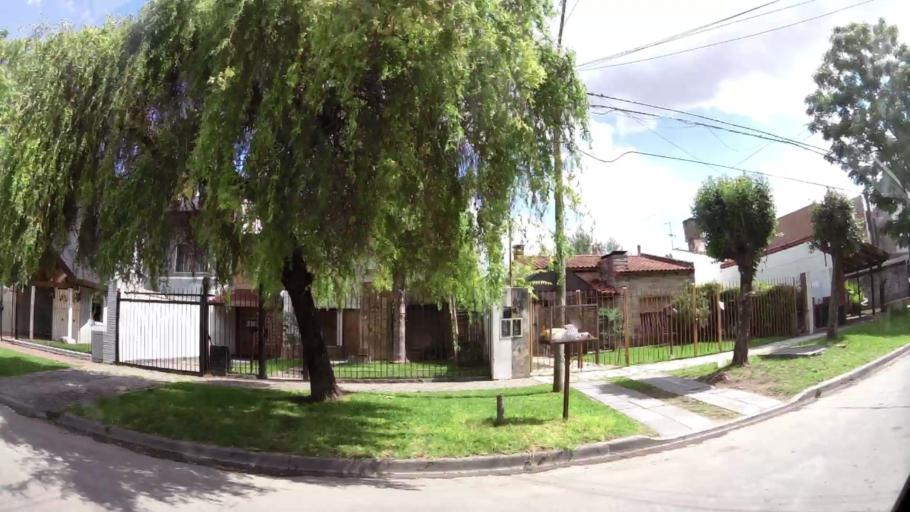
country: AR
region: Buenos Aires
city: Ituzaingo
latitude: -34.6463
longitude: -58.6600
